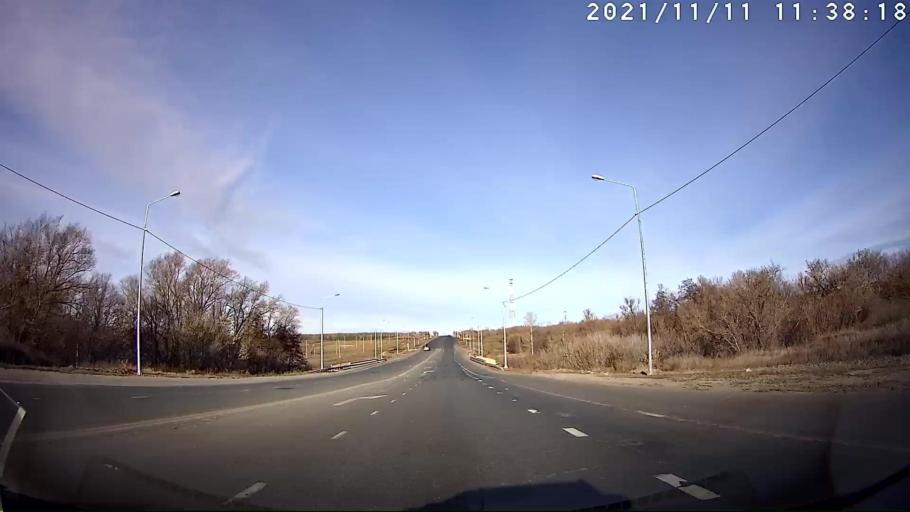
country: RU
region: Samara
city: Varlamovo
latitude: 53.3807
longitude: 48.3771
